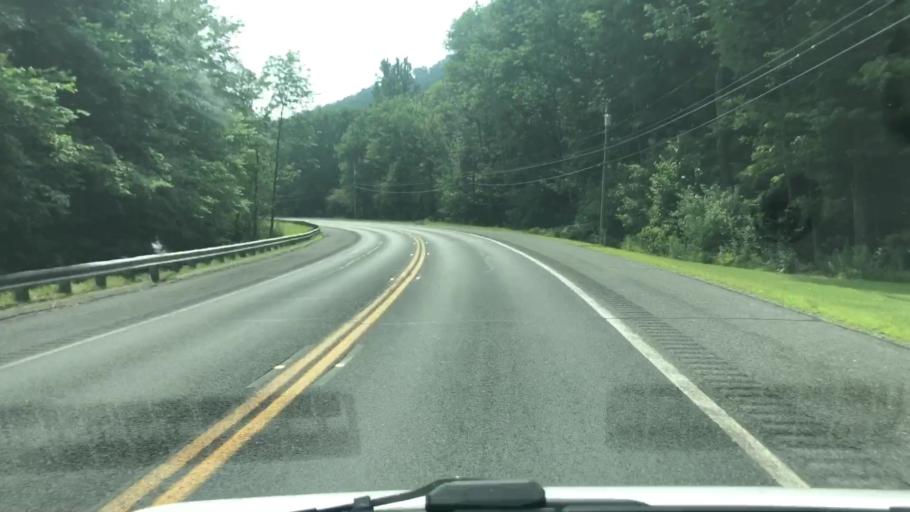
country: US
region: Massachusetts
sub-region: Berkshire County
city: Williamstown
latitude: 42.6249
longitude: -73.2311
